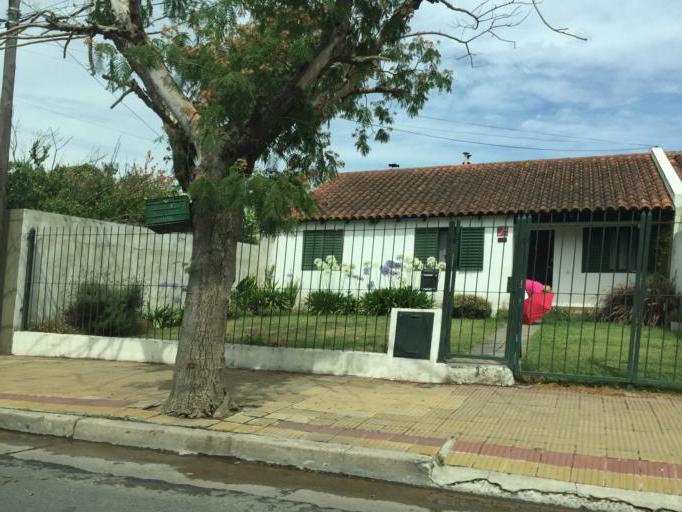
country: AR
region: Buenos Aires
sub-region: Partido de Tandil
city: Tandil
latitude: -37.3223
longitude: -59.1086
